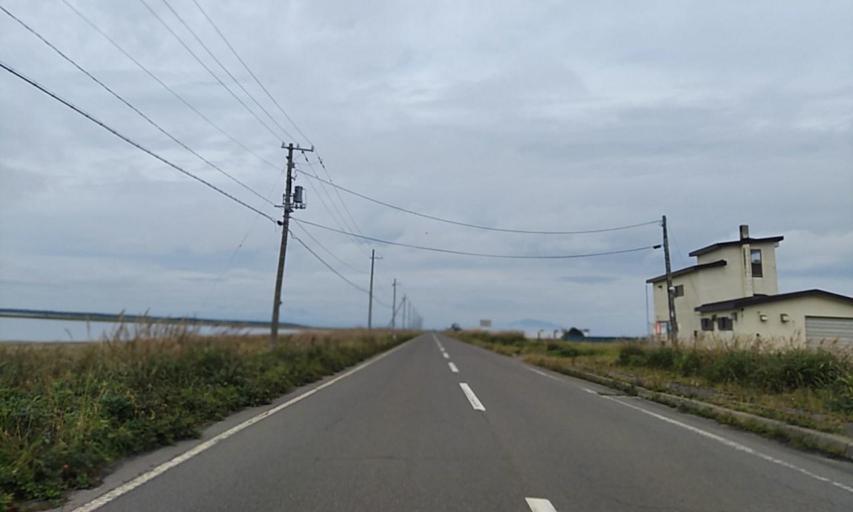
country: JP
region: Hokkaido
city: Shibetsu
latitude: 43.5935
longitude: 145.3298
